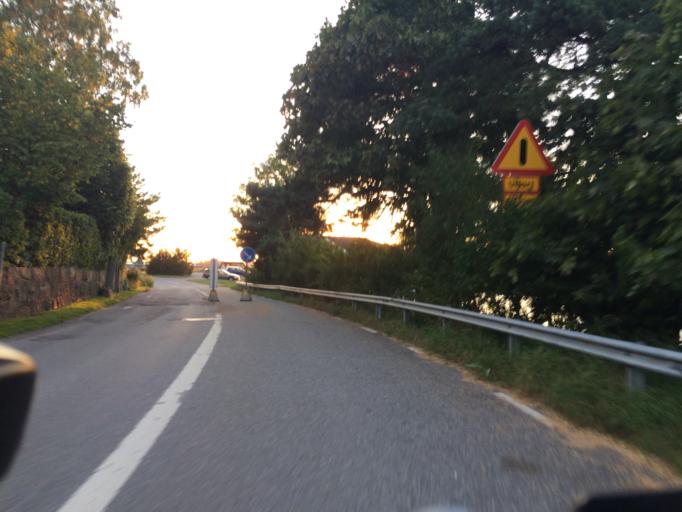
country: SE
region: Soedermanland
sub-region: Eskilstuna Kommun
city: Kvicksund
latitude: 59.4517
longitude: 16.3231
